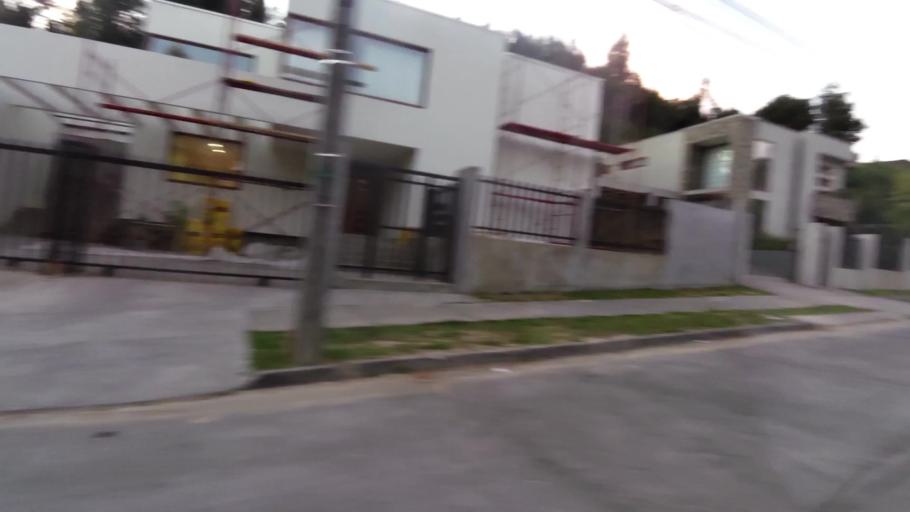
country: CL
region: Biobio
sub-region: Provincia de Concepcion
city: Concepcion
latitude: -36.8643
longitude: -73.0395
